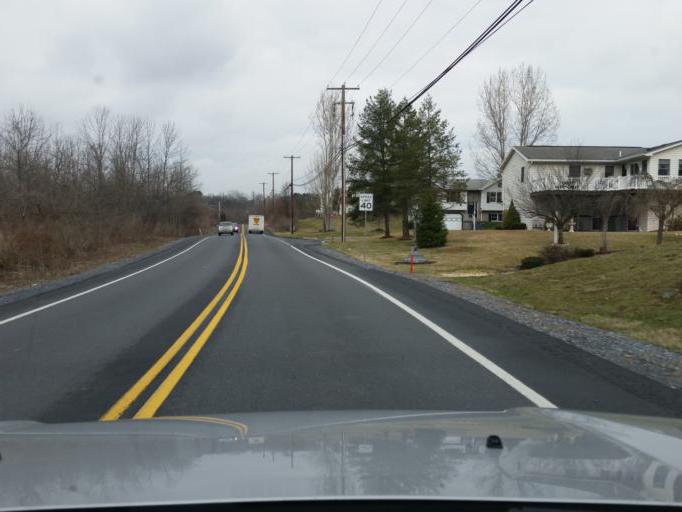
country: US
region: Pennsylvania
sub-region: Dauphin County
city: Paxtonia
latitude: 40.3048
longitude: -76.7661
